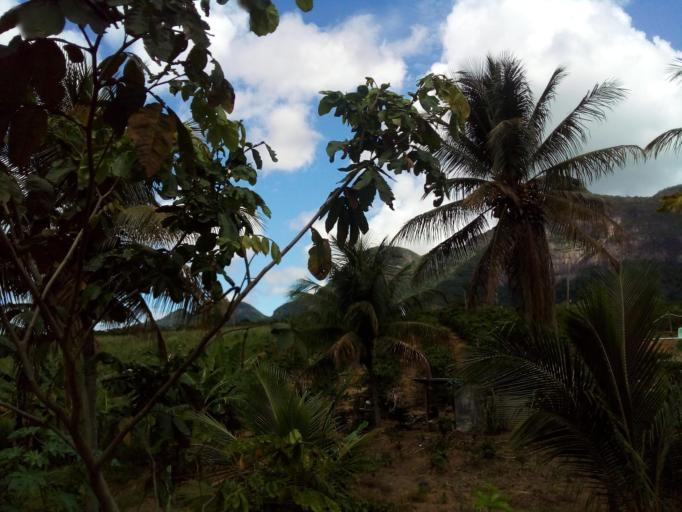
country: BR
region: Espirito Santo
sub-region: Ibiracu
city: Ibiracu
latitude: -19.8880
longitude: -40.3642
